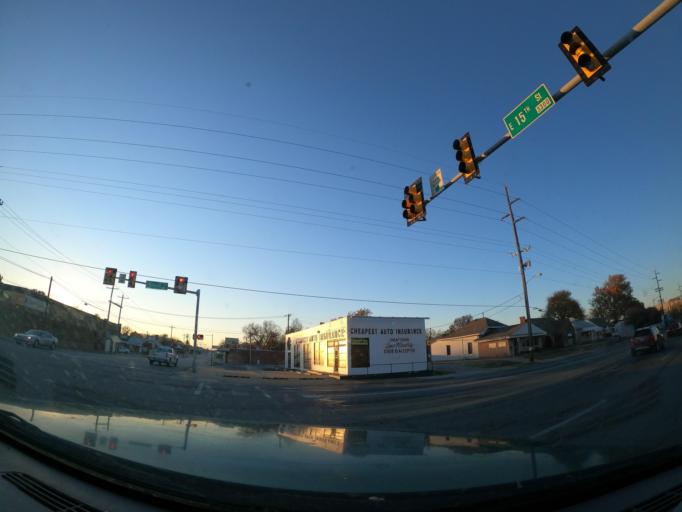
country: US
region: Oklahoma
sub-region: Tulsa County
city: Tulsa
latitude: 36.1407
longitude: -95.9403
